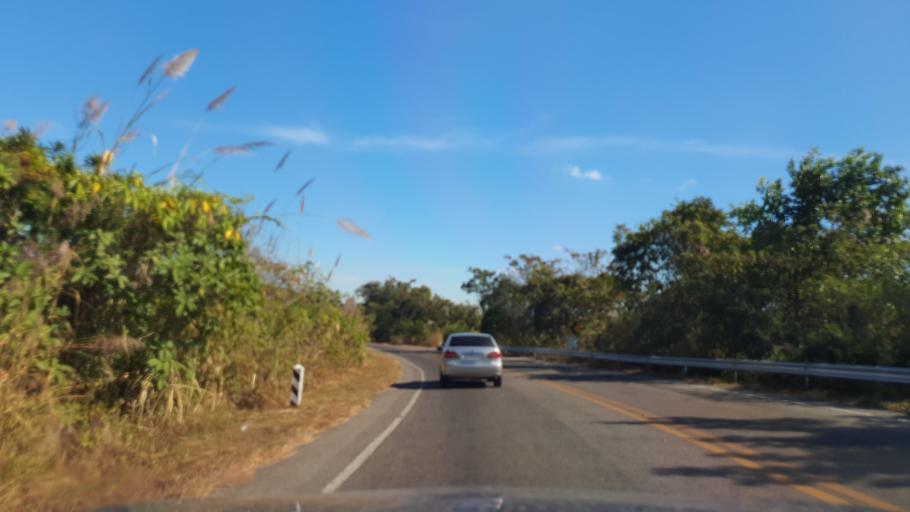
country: TH
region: Kalasin
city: Khao Wong
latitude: 16.7927
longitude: 104.1385
